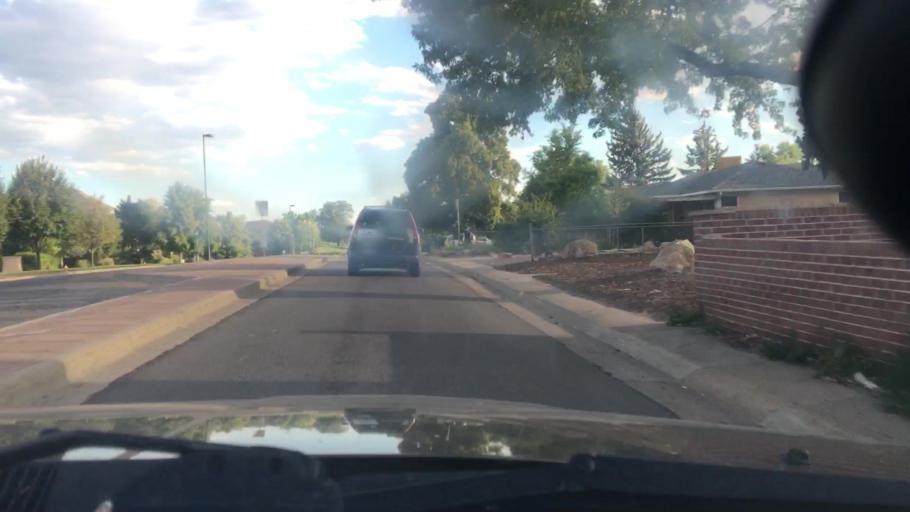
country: US
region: Colorado
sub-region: Arapahoe County
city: Glendale
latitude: 39.7315
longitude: -104.9035
